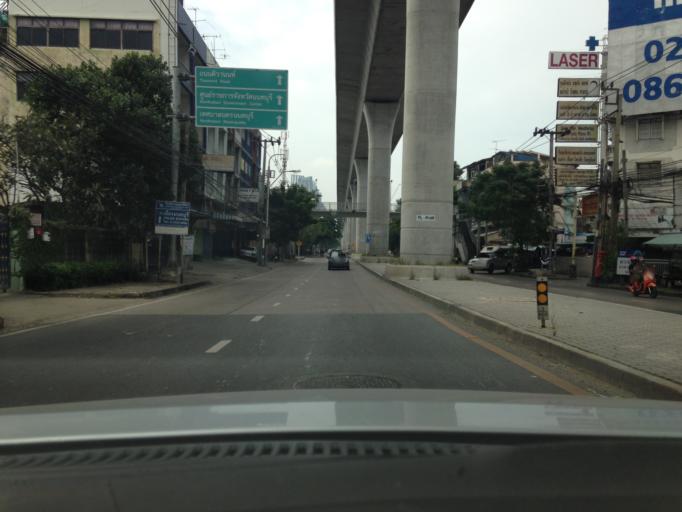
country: TH
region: Nonthaburi
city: Mueang Nonthaburi
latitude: 13.8339
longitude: 100.5215
